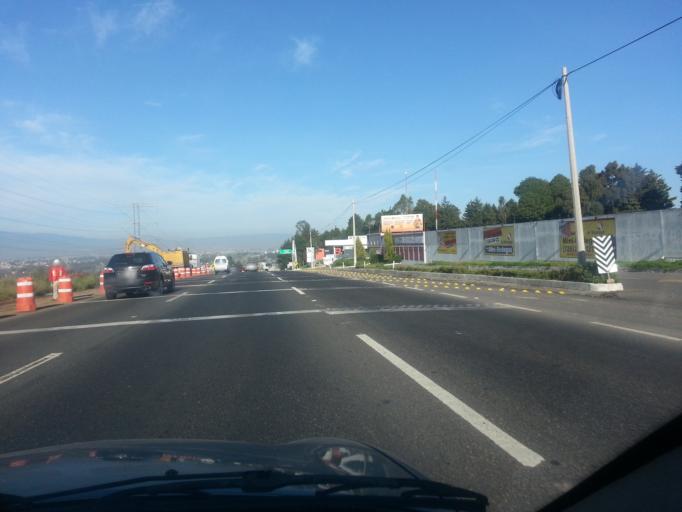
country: MX
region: Mexico
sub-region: Lerma
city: Fraccionamiento y Club de Golf los Encinos
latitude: 19.2823
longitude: -99.4805
